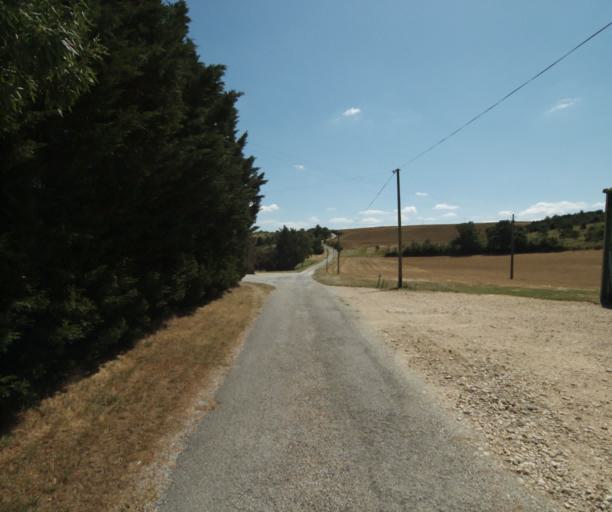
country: FR
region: Midi-Pyrenees
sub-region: Departement de la Haute-Garonne
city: Saint-Felix-Lauragais
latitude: 43.4598
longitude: 1.8850
